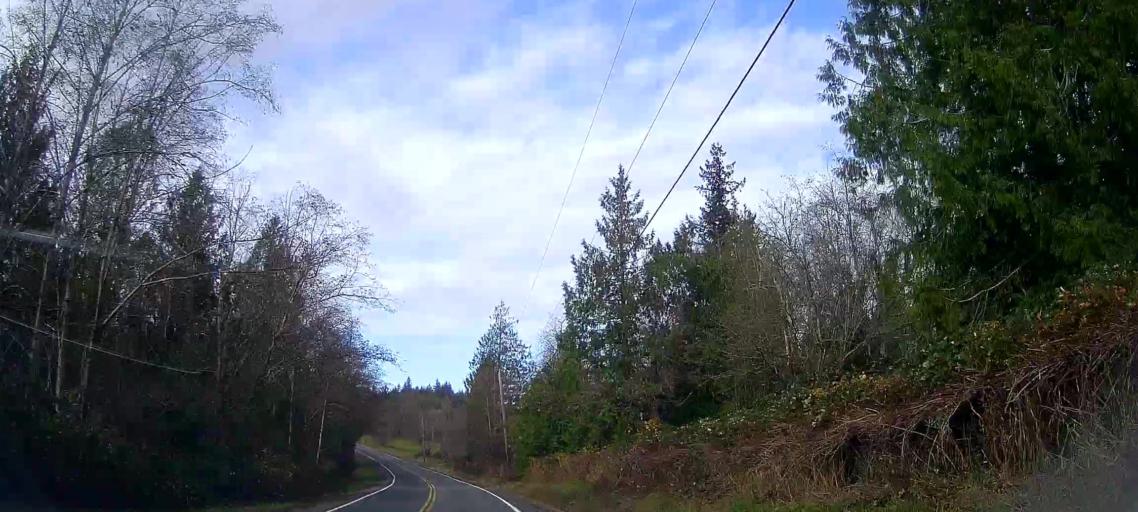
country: US
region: Washington
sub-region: Skagit County
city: Big Lake
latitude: 48.4146
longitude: -122.2231
